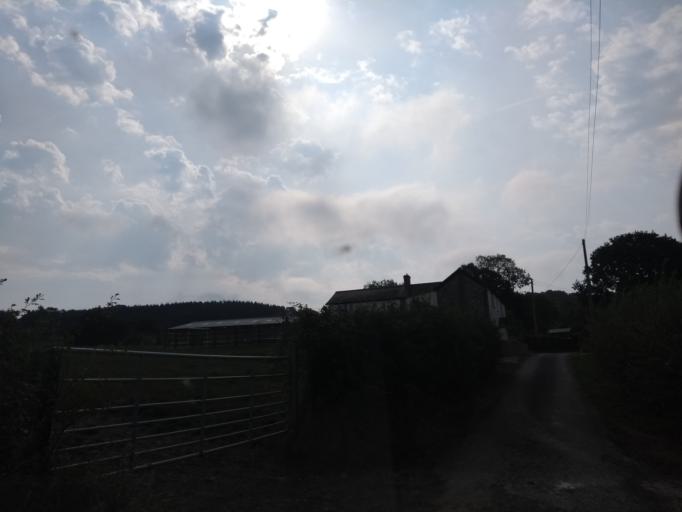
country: GB
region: England
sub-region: Somerset
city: Chard
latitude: 50.8832
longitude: -3.0434
